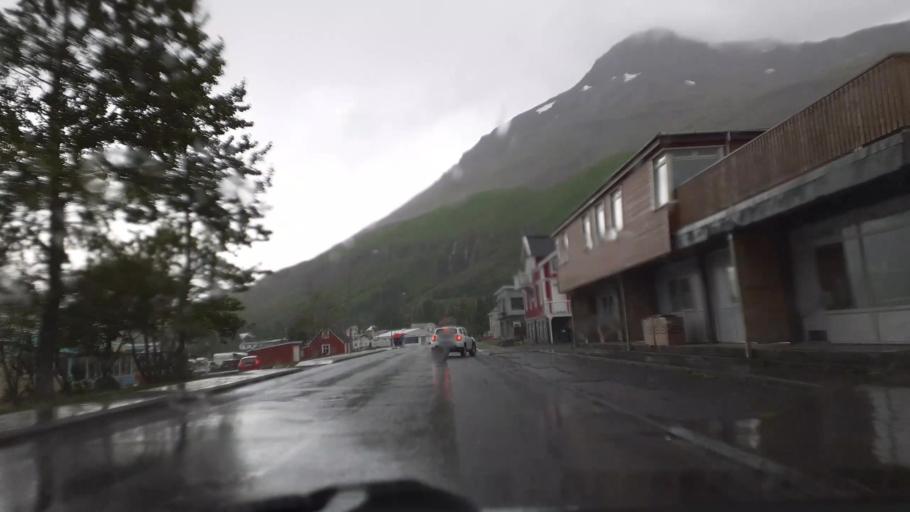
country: IS
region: East
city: Eskifjoerdur
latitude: 65.2609
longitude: -14.0031
